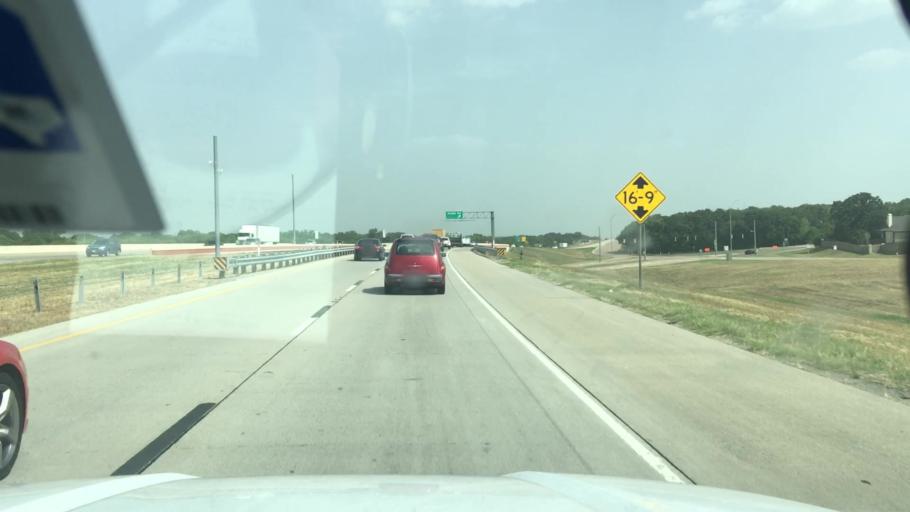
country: US
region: Texas
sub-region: Tarrant County
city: Grapevine
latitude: 32.8929
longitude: -97.0835
